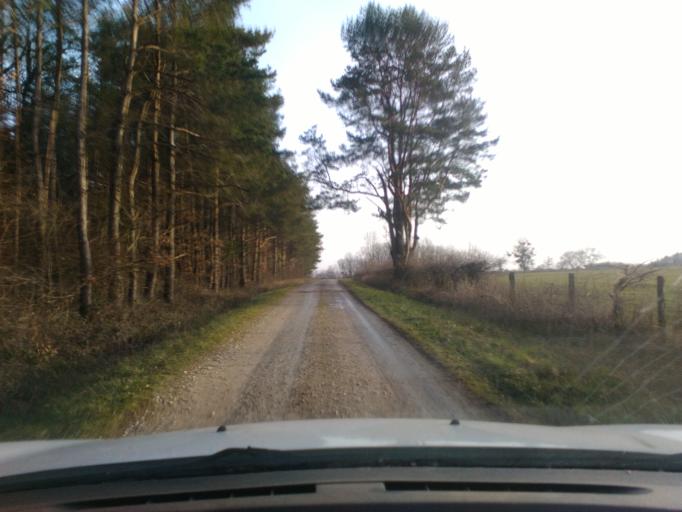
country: FR
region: Lorraine
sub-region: Departement des Vosges
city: Vittel
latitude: 48.2627
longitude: 6.0013
